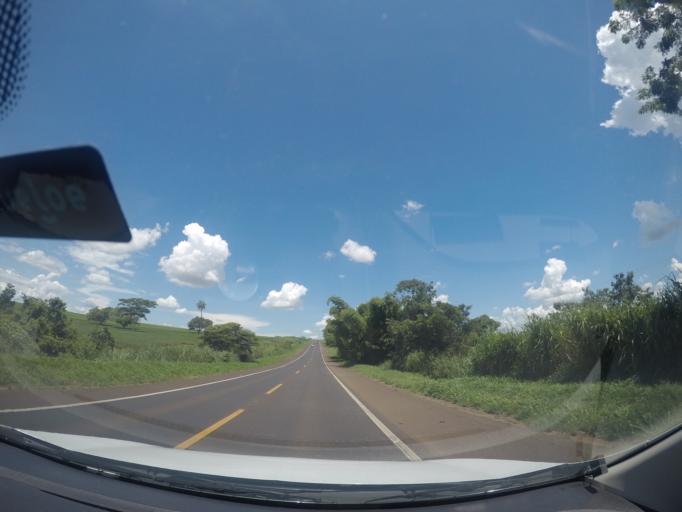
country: BR
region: Minas Gerais
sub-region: Prata
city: Prata
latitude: -19.4892
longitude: -48.8589
